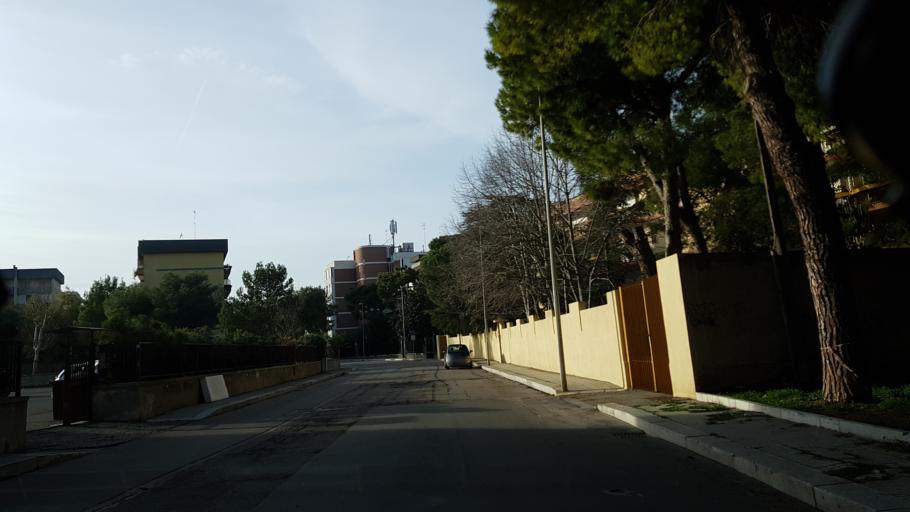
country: IT
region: Apulia
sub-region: Provincia di Brindisi
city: Brindisi
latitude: 40.6178
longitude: 17.9233
